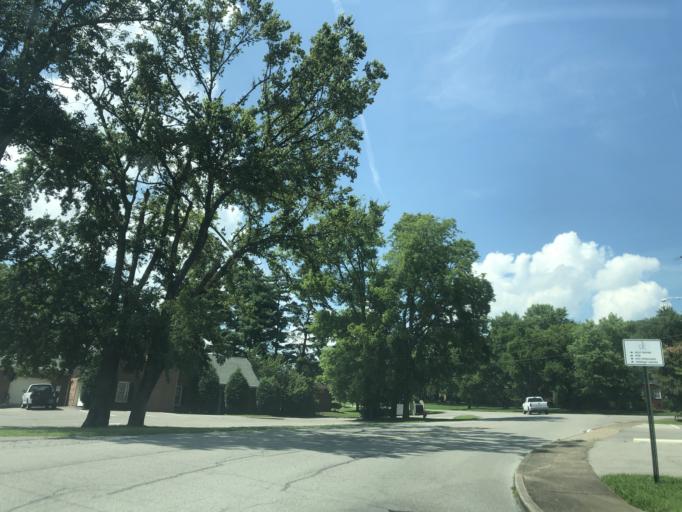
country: US
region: Tennessee
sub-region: Davidson County
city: Lakewood
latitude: 36.1710
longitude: -86.6705
